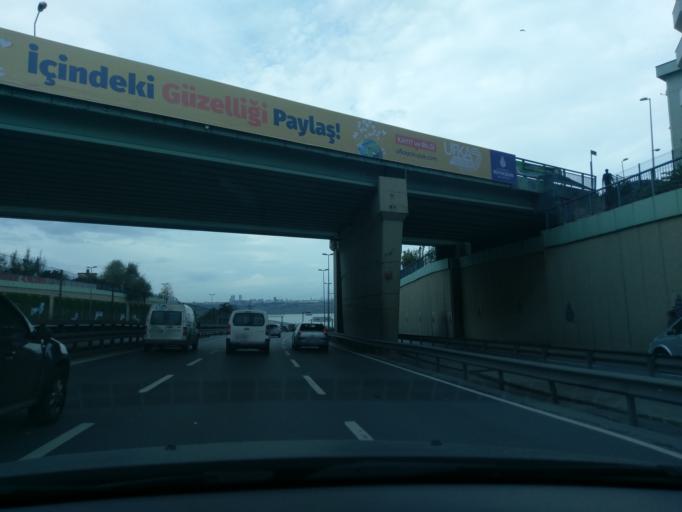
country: TR
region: Istanbul
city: Bahcelievler
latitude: 40.9855
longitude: 28.7796
